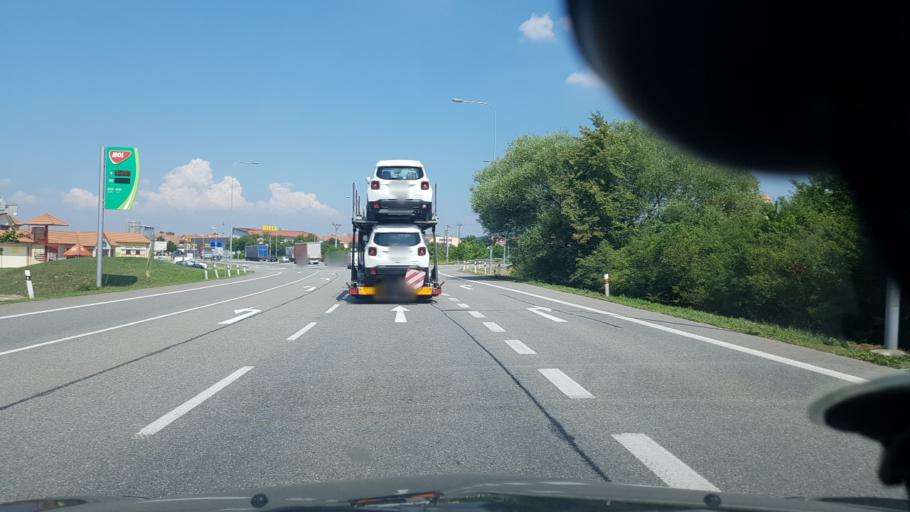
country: CZ
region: South Moravian
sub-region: Okres Breclav
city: Mikulov
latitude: 48.7981
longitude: 16.6331
